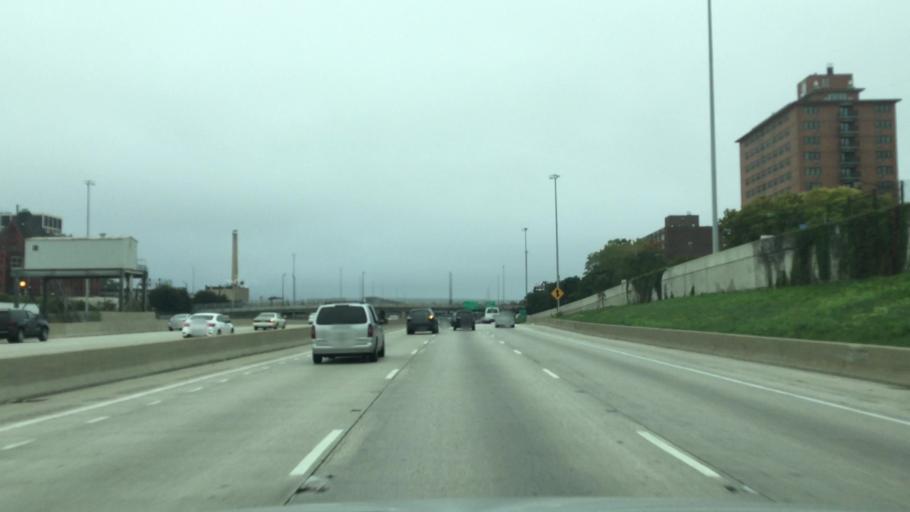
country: US
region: Illinois
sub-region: Cook County
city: Chicago
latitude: 41.8374
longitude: -87.6313
